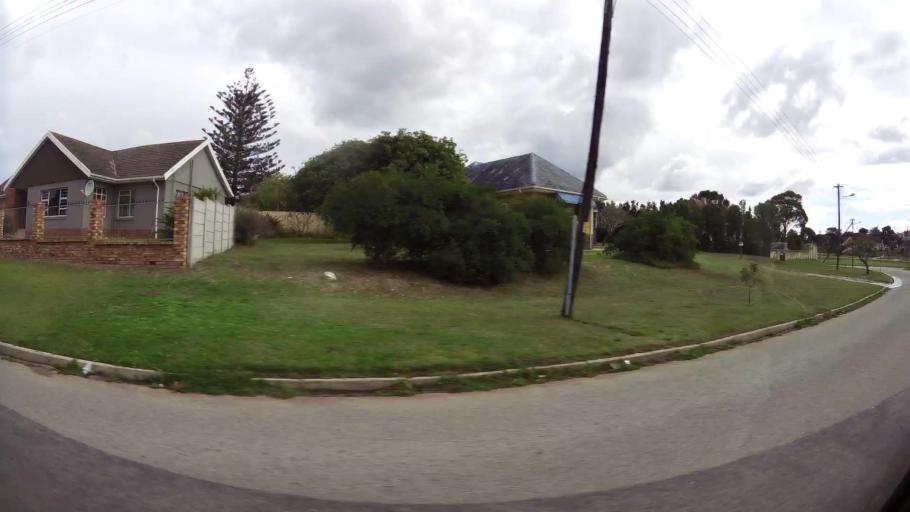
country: ZA
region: Eastern Cape
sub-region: Nelson Mandela Bay Metropolitan Municipality
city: Port Elizabeth
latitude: -33.9381
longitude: 25.5185
